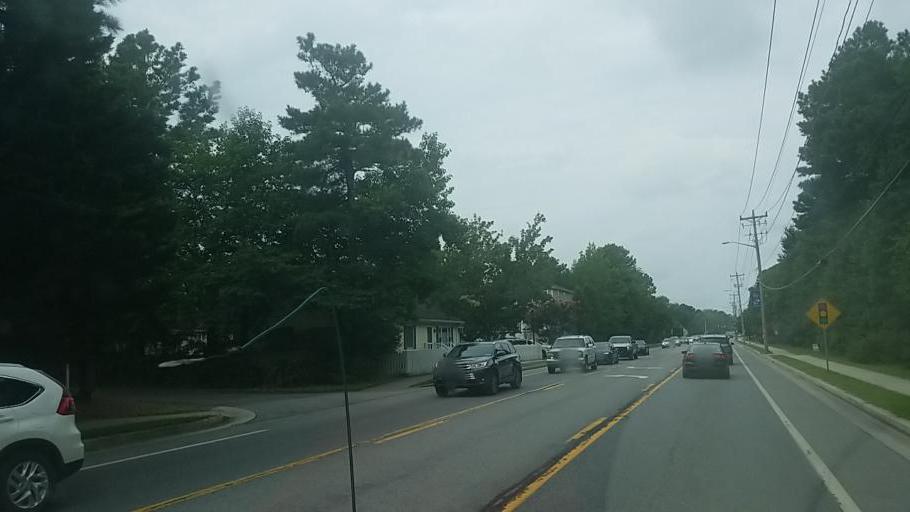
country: US
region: Delaware
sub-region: Sussex County
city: Bethany Beach
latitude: 38.5388
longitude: -75.0632
